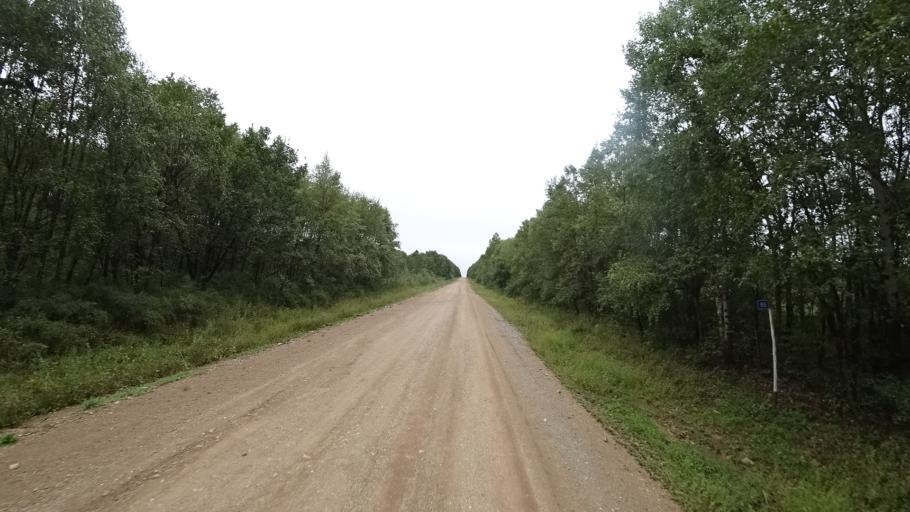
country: RU
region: Primorskiy
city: Ivanovka
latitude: 44.0263
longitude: 132.5255
